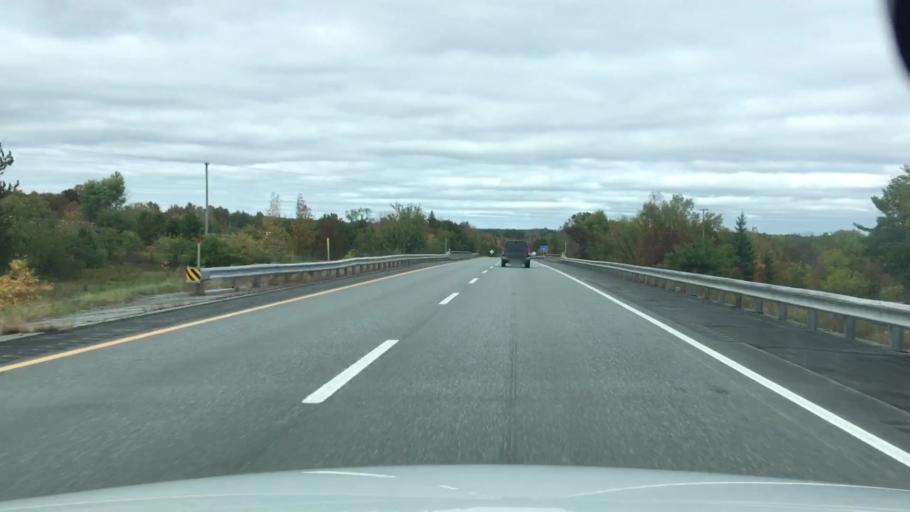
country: US
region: Maine
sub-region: Somerset County
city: Pittsfield
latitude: 44.7687
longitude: -69.4103
